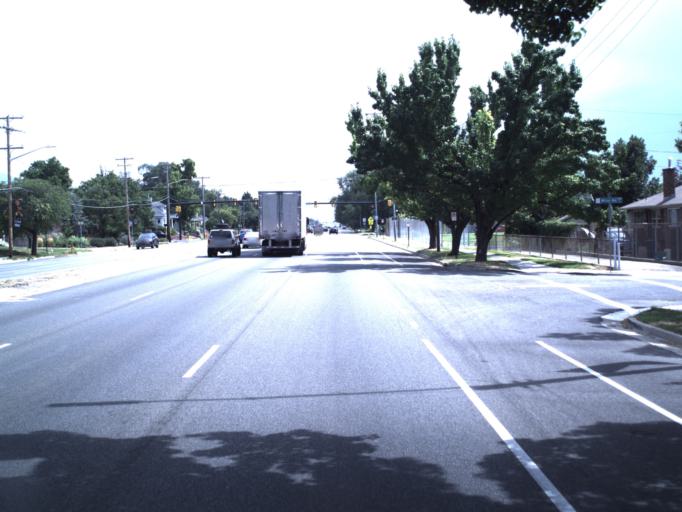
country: US
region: Utah
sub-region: Salt Lake County
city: South Salt Lake
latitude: 40.7351
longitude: -111.8713
